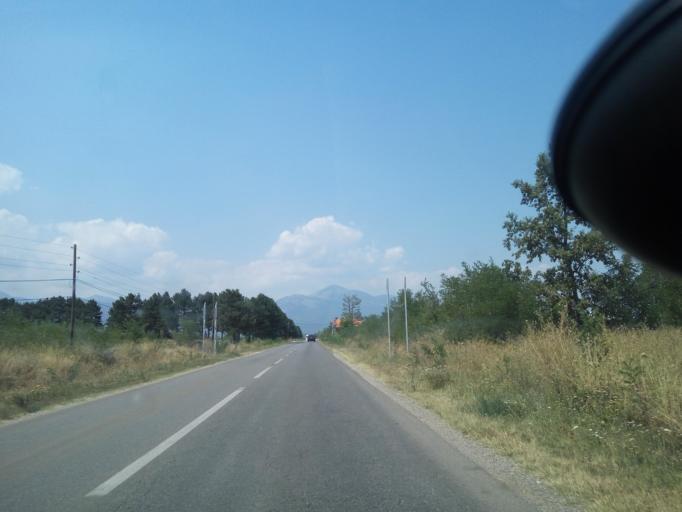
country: XK
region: Gjakova
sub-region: Komuna e Decanit
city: Gllogjan
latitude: 42.4703
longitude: 20.3436
